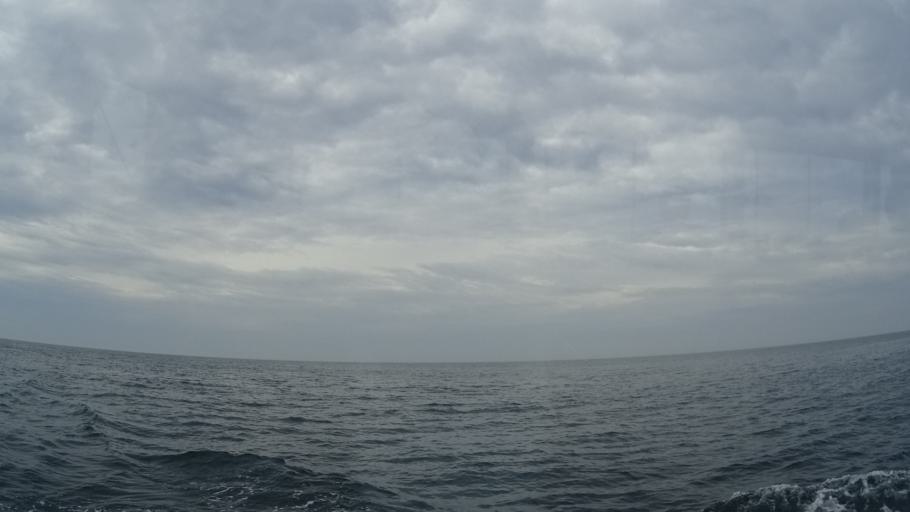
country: JP
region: Fukui
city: Mikuni
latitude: 36.2536
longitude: 136.1172
